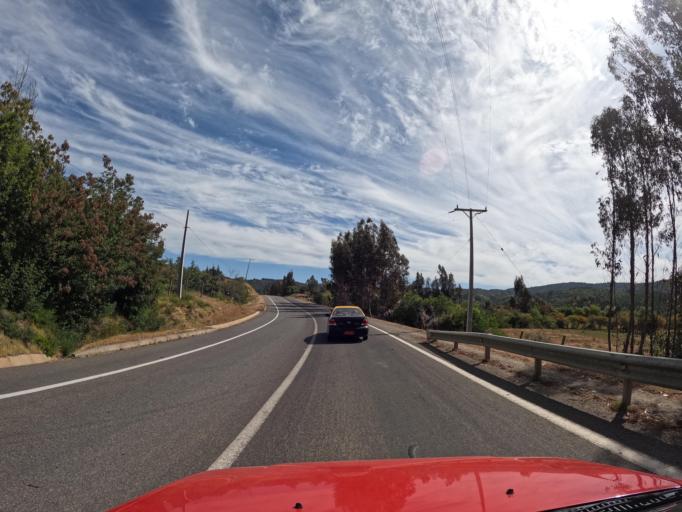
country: CL
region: Maule
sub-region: Provincia de Talca
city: Talca
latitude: -35.1313
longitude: -71.9592
